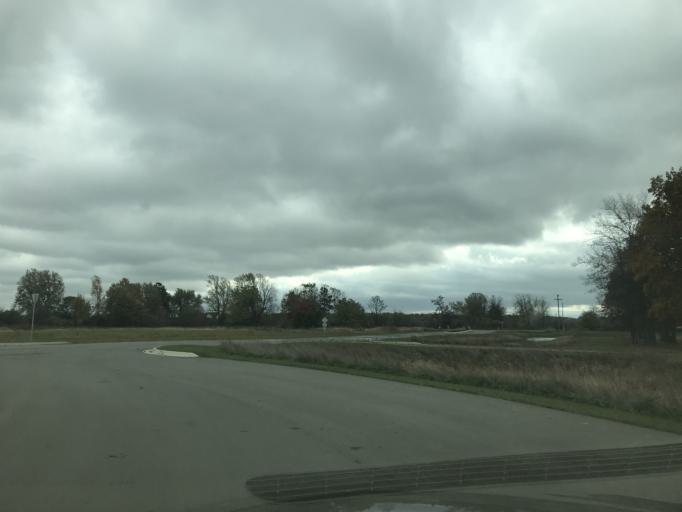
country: US
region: Michigan
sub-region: Eaton County
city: Grand Ledge
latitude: 42.7138
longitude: -84.6937
